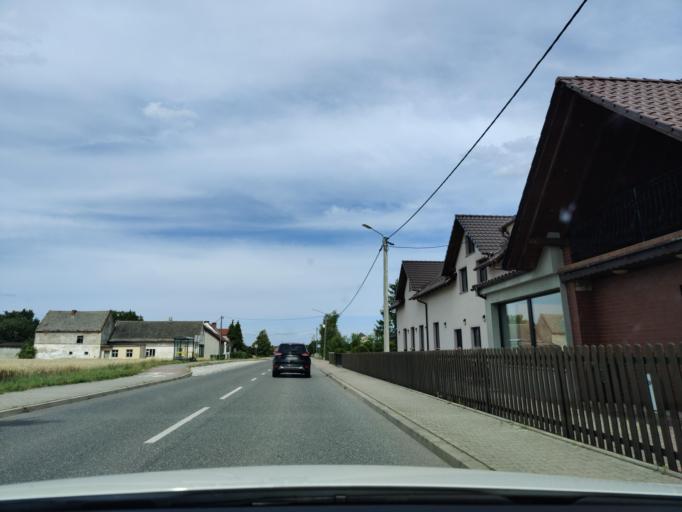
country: PL
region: Opole Voivodeship
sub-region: Powiat prudnicki
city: Biala
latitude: 50.4137
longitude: 17.7181
